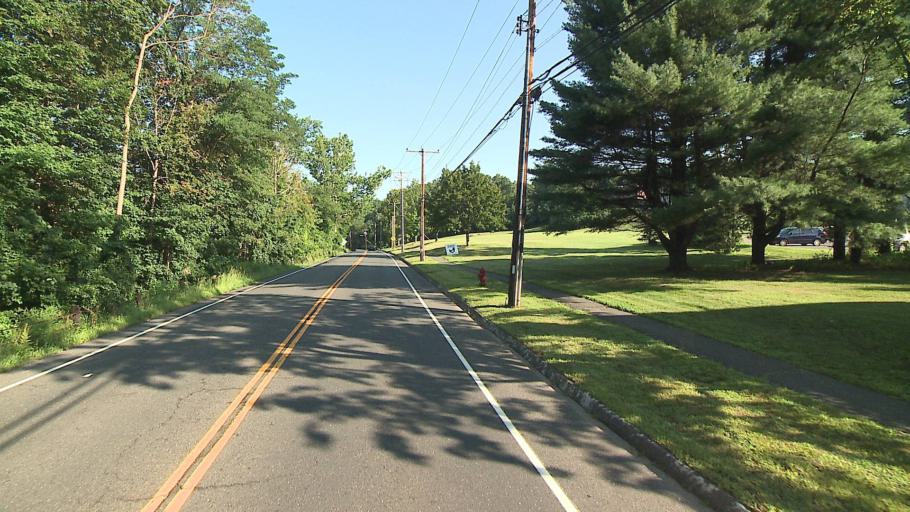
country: US
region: Connecticut
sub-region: Hartford County
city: Farmington
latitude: 41.7490
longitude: -72.8690
